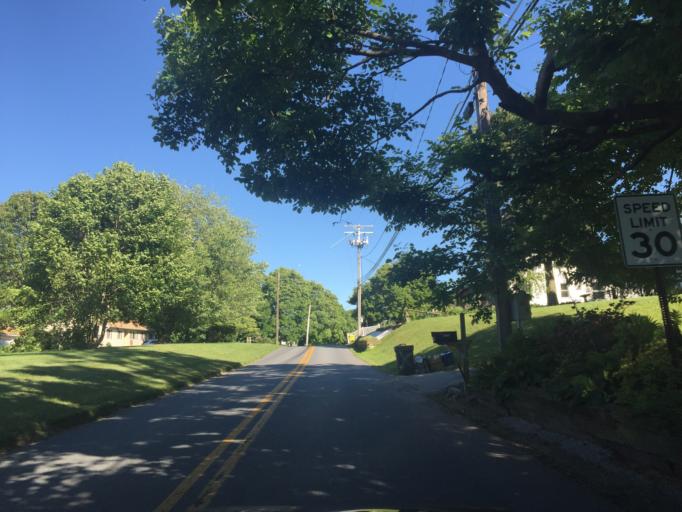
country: US
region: Maryland
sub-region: Carroll County
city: Hampstead
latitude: 39.5454
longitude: -76.8367
